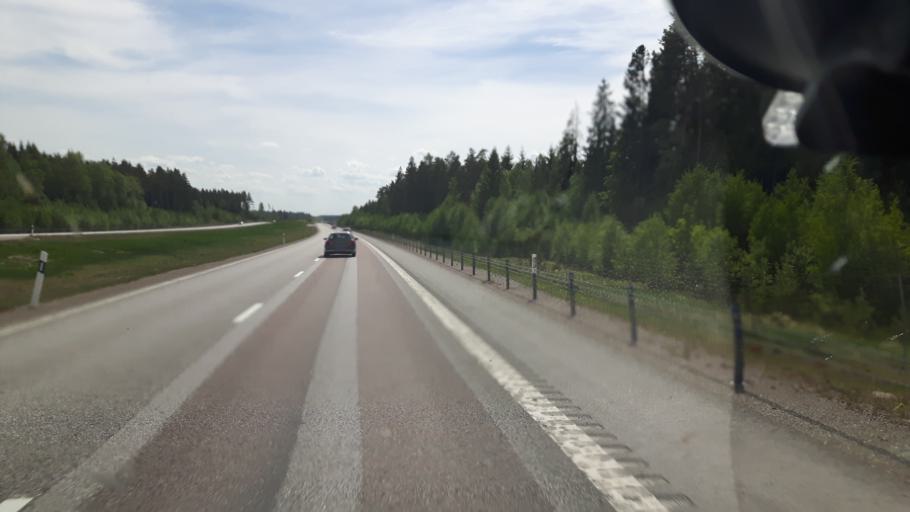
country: SE
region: Uppsala
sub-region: Tierps Kommun
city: Tierp
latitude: 60.2765
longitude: 17.5013
